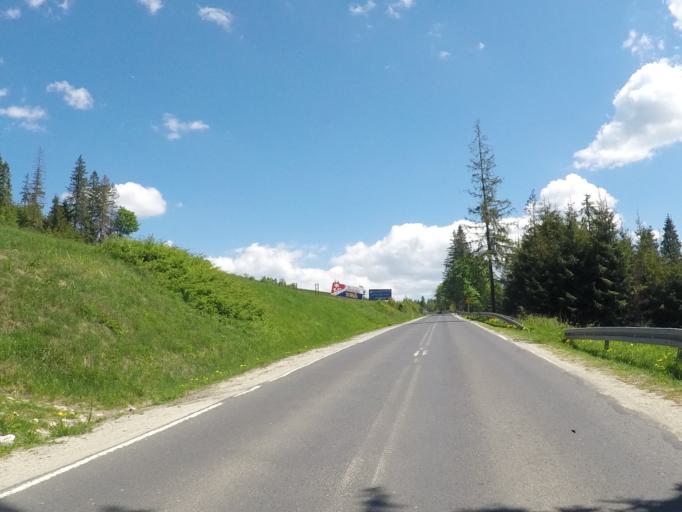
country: PL
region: Lesser Poland Voivodeship
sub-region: Powiat tatrzanski
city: Bukowina Tatrzanska
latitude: 49.3323
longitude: 20.0826
